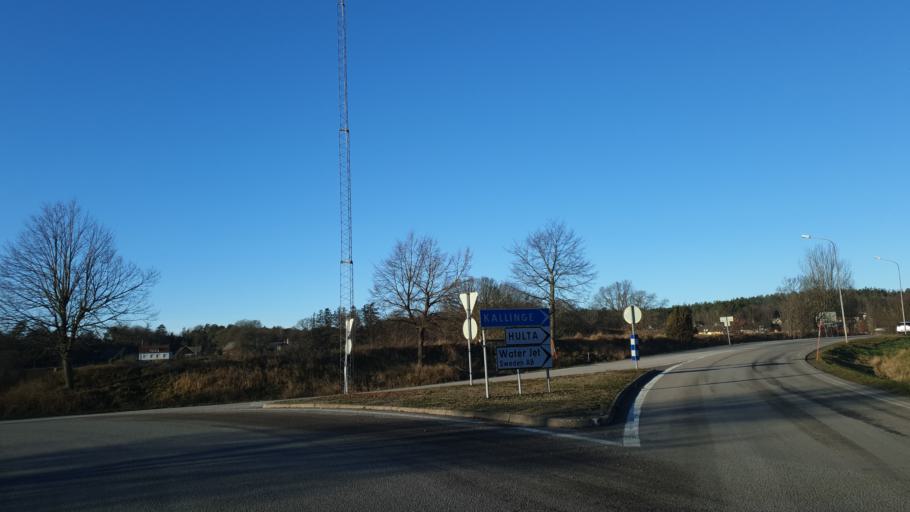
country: SE
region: Blekinge
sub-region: Ronneby Kommun
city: Ronneby
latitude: 56.2022
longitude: 15.3104
